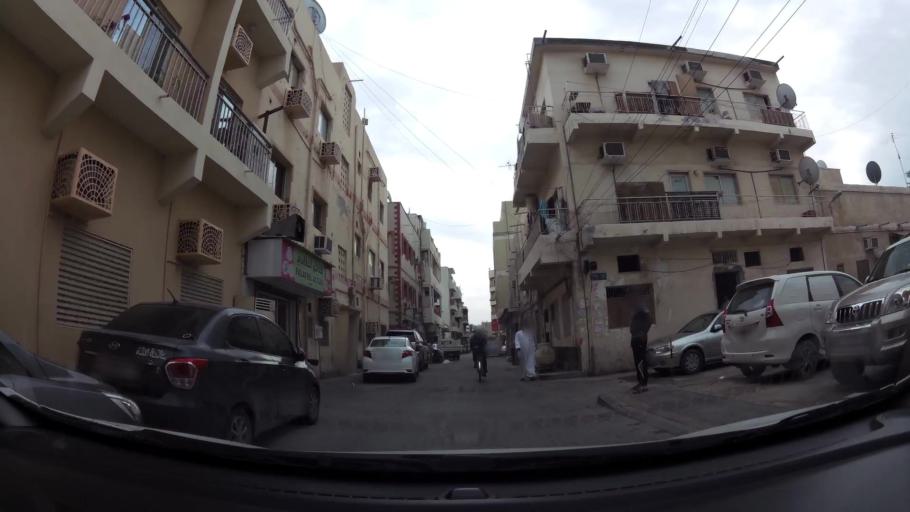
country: BH
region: Manama
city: Manama
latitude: 26.2254
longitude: 50.5910
